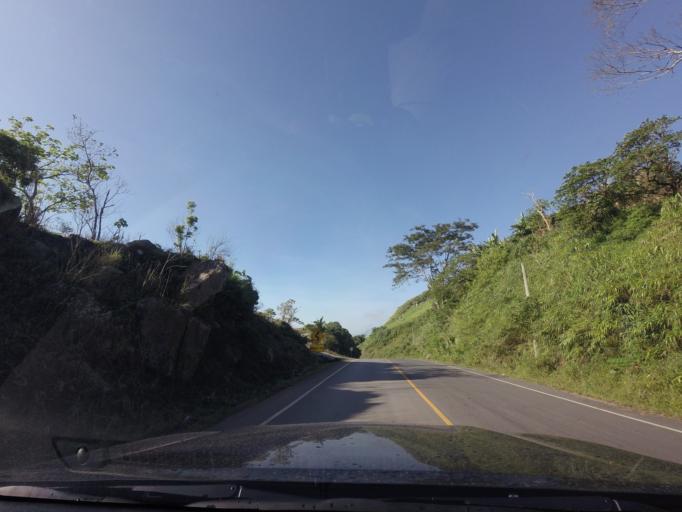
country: TH
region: Phetchabun
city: Lom Kao
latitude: 16.8808
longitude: 101.1024
